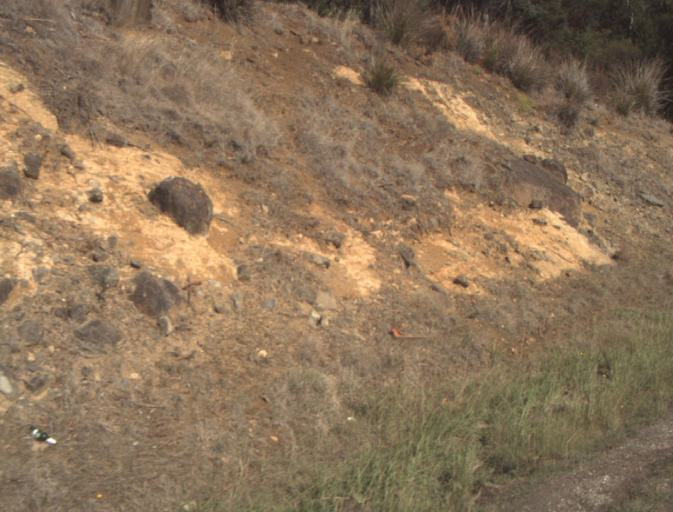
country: AU
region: Tasmania
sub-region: Launceston
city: Mayfield
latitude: -41.2639
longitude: 147.2166
